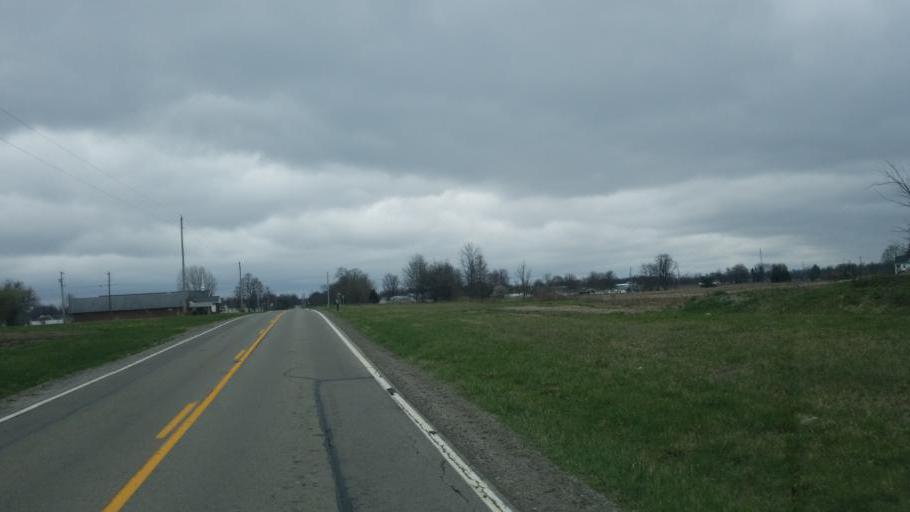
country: US
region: Ohio
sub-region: Hardin County
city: Kenton
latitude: 40.6682
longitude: -83.6008
